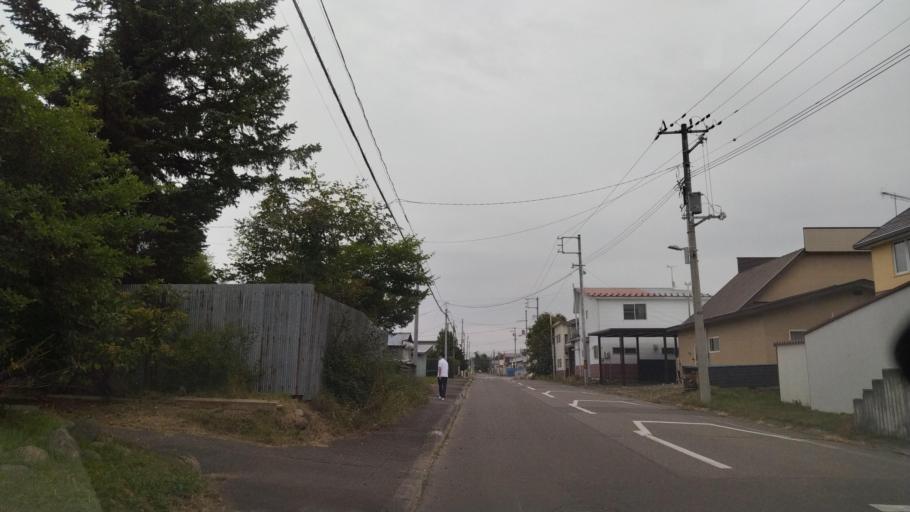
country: JP
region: Hokkaido
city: Otofuke
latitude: 43.2314
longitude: 143.2816
